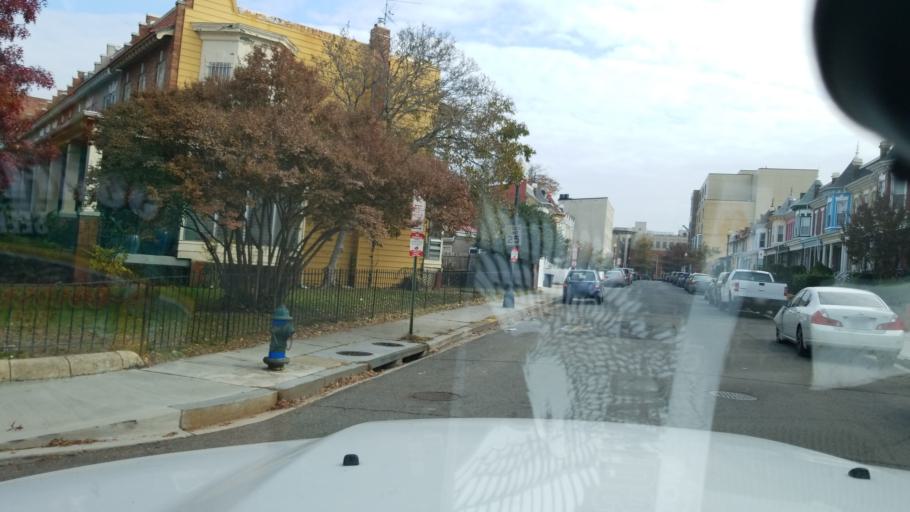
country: US
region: Washington, D.C.
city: Washington, D.C.
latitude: 38.9333
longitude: -77.0263
